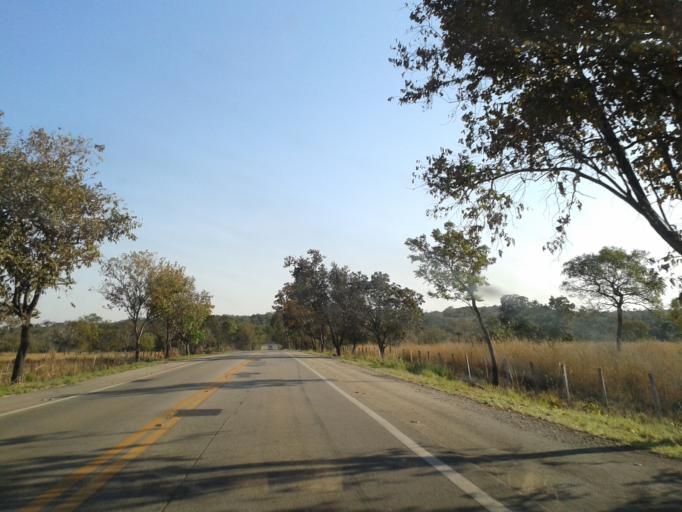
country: BR
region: Goias
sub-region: Itapuranga
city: Itapuranga
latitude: -15.4126
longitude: -50.3778
